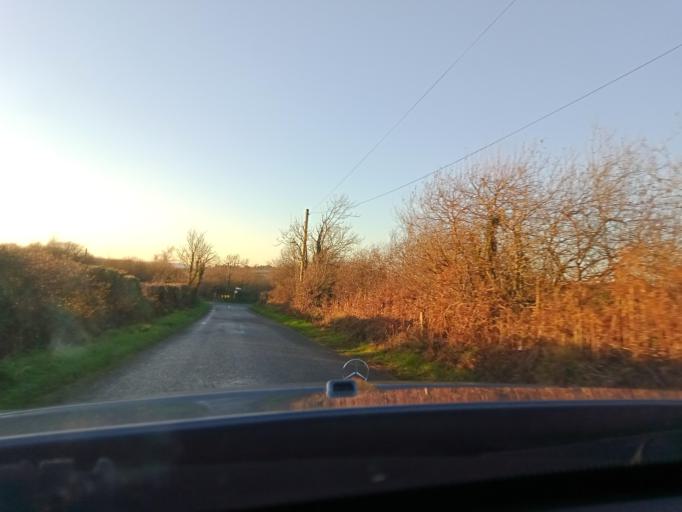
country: IE
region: Munster
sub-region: Waterford
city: Waterford
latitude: 52.3672
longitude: -7.1195
